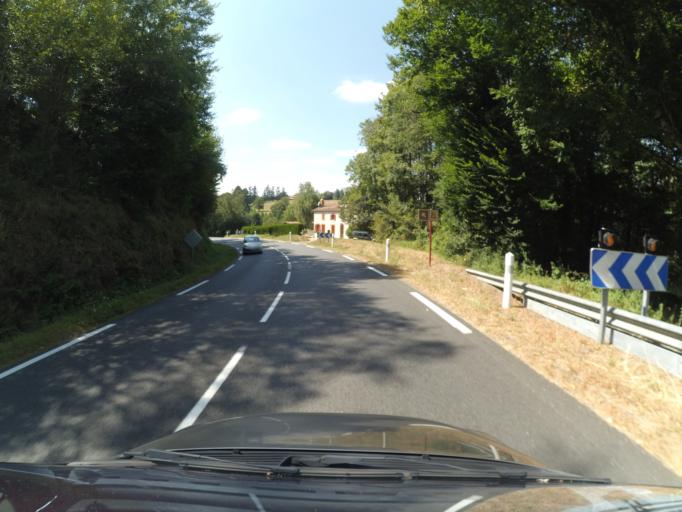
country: FR
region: Limousin
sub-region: Departement de la Haute-Vienne
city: Bussiere-Poitevine
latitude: 46.2340
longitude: 0.9357
